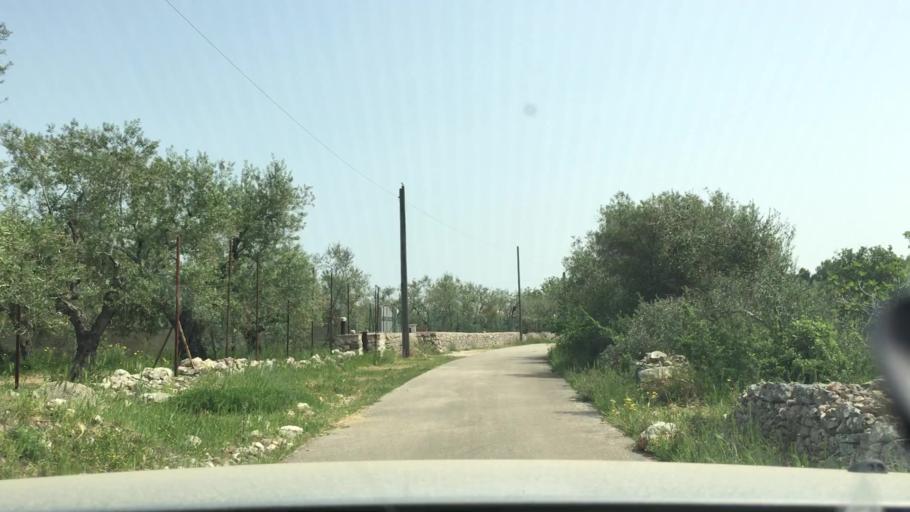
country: IT
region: Apulia
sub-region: Provincia di Barletta - Andria - Trani
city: Capirro
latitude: 41.2554
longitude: 16.4562
